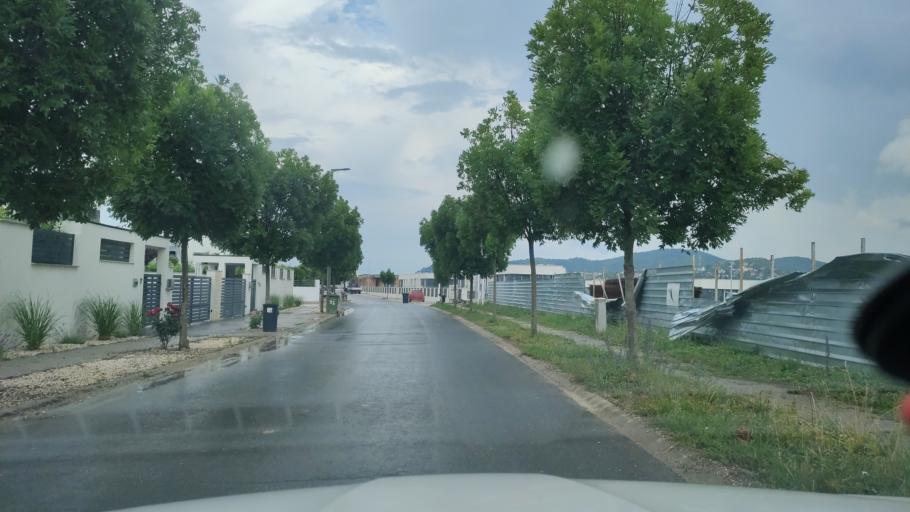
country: HU
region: Pest
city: Toeroekbalint
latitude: 47.4422
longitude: 18.9295
